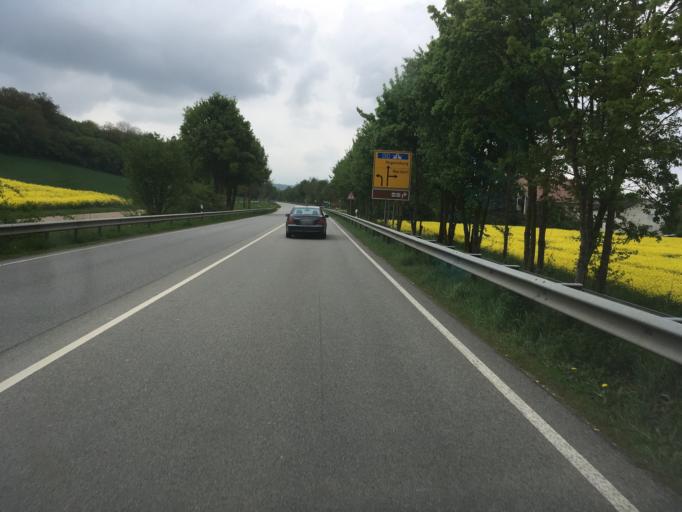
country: DE
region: Bavaria
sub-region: Upper Palatinate
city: Sinzing
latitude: 49.0182
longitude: 12.0264
